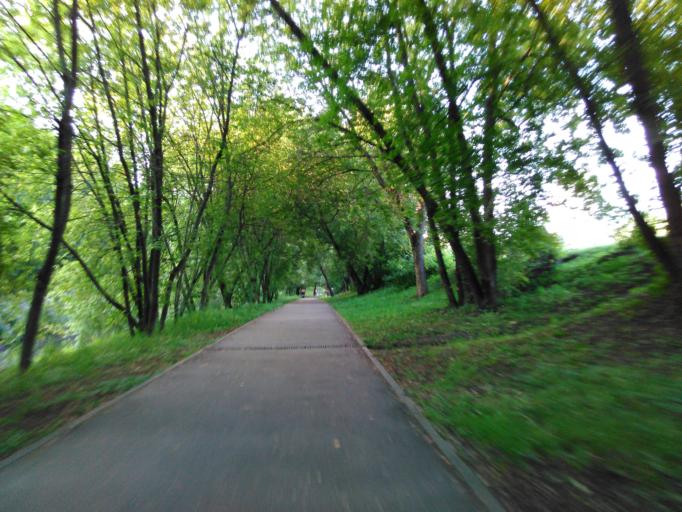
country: RU
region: Moscow
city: Vorob'yovo
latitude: 55.7257
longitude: 37.5192
